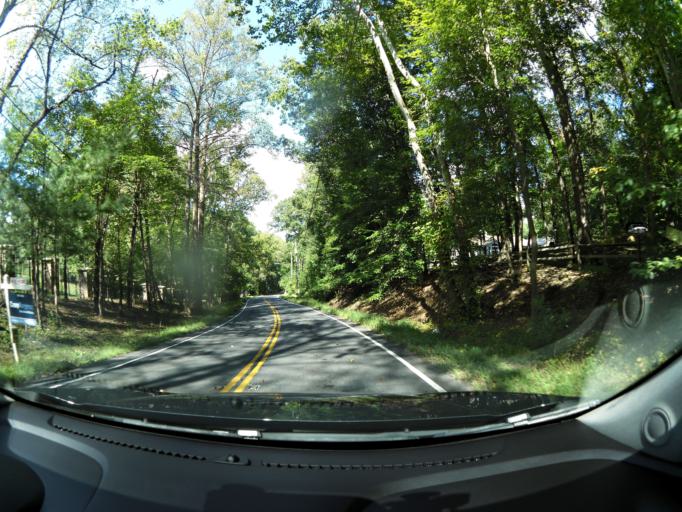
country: US
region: Virginia
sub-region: Fairfax County
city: Great Falls
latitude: 38.9729
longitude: -77.2428
